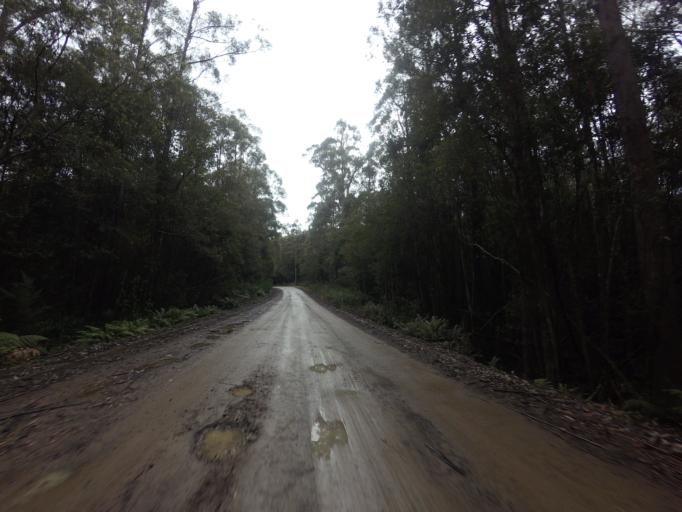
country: AU
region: Tasmania
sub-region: Huon Valley
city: Geeveston
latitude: -43.5054
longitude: 146.8767
